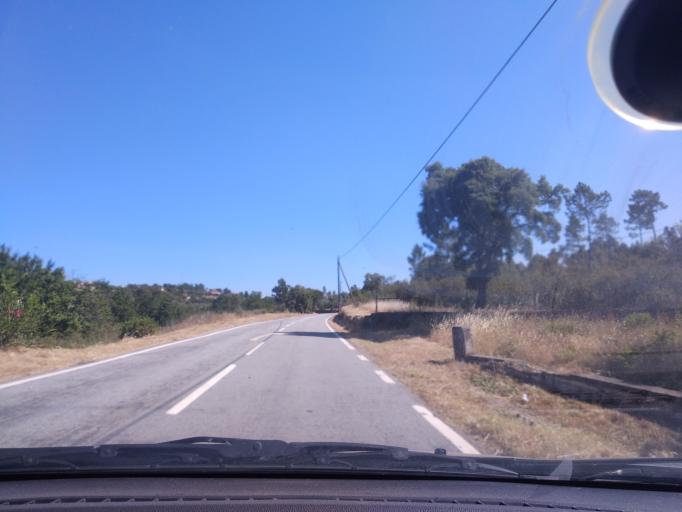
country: ES
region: Extremadura
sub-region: Provincia de Caceres
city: Cedillo
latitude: 39.7397
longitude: -7.6211
